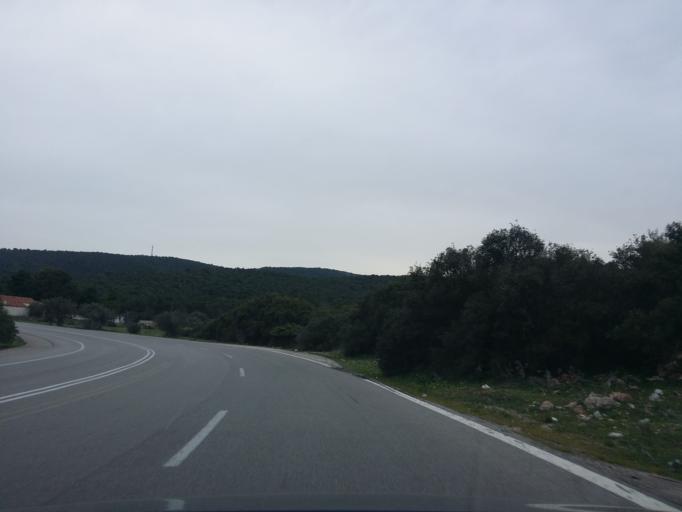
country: GR
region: Attica
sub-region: Nomarchia Dytikis Attikis
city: Vilia
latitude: 38.1479
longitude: 23.4238
